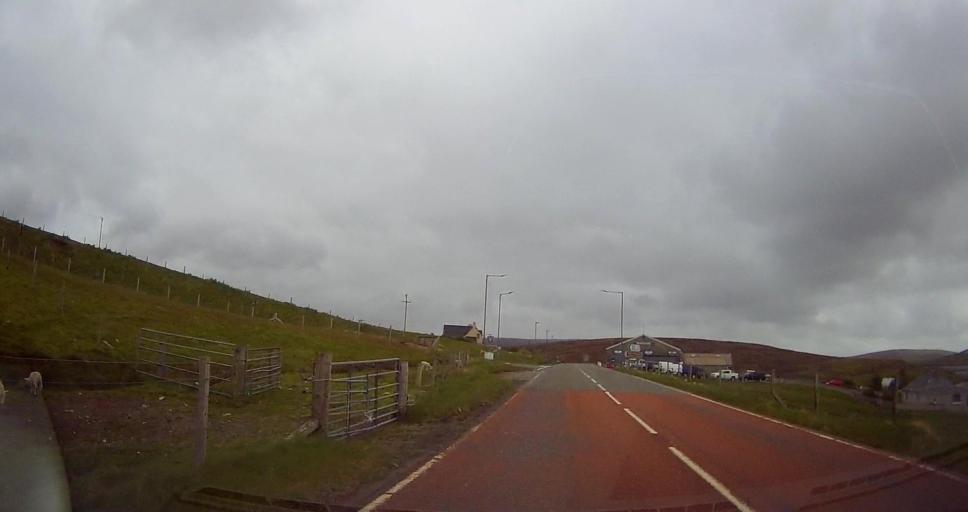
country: GB
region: Scotland
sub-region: Shetland Islands
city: Lerwick
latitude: 60.2545
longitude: -1.4064
